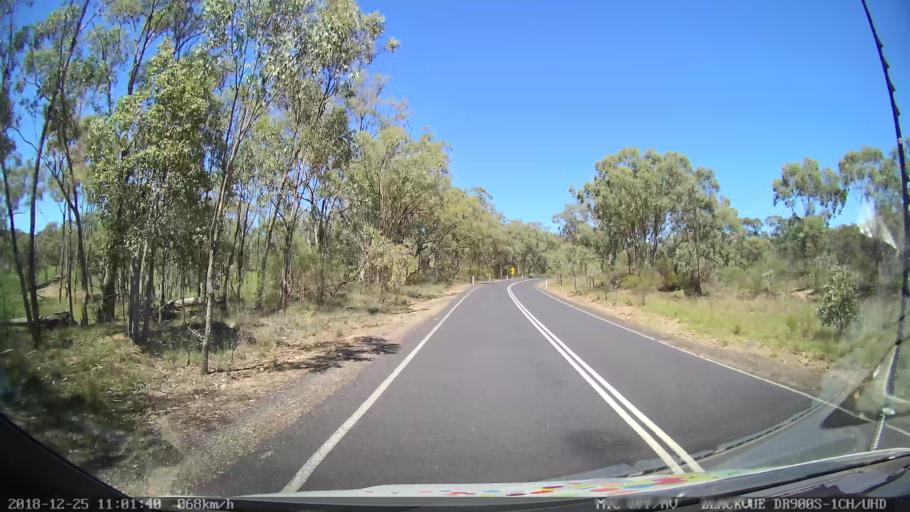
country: AU
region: New South Wales
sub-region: Upper Hunter Shire
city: Merriwa
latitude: -32.4058
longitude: 150.1992
